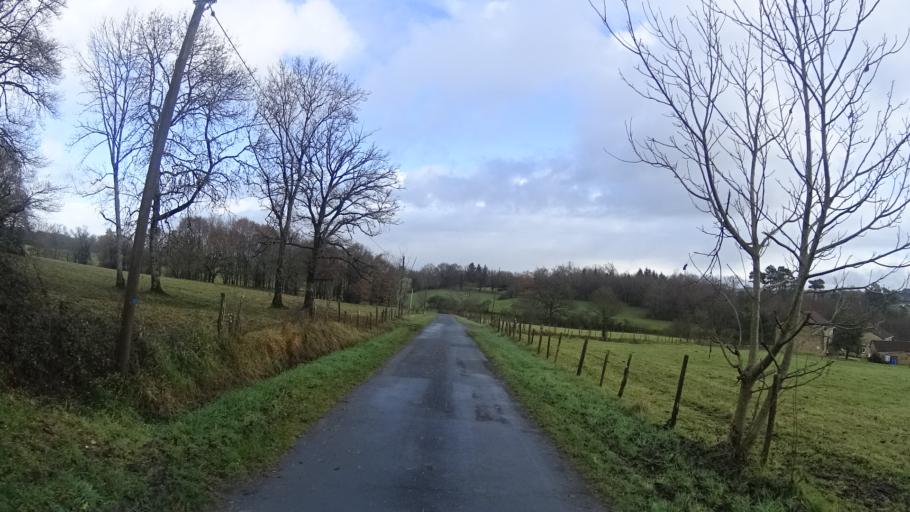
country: FR
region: Aquitaine
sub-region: Departement de la Dordogne
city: Thiviers
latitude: 45.4090
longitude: 0.9660
